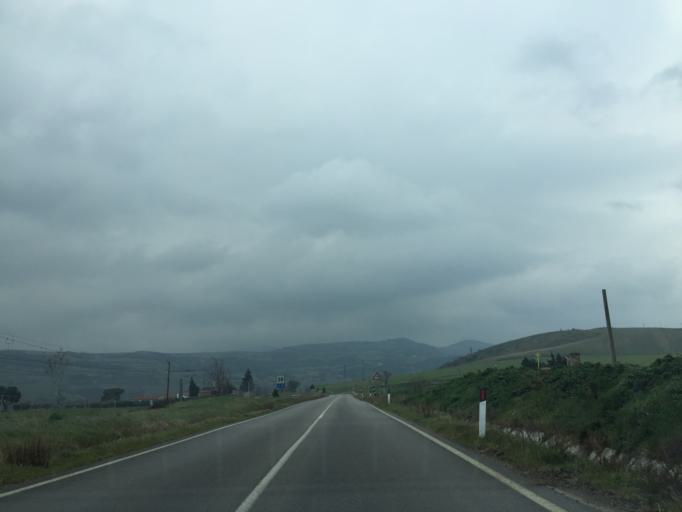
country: IT
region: Apulia
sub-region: Provincia di Foggia
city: Bovino
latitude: 41.2882
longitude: 15.3801
